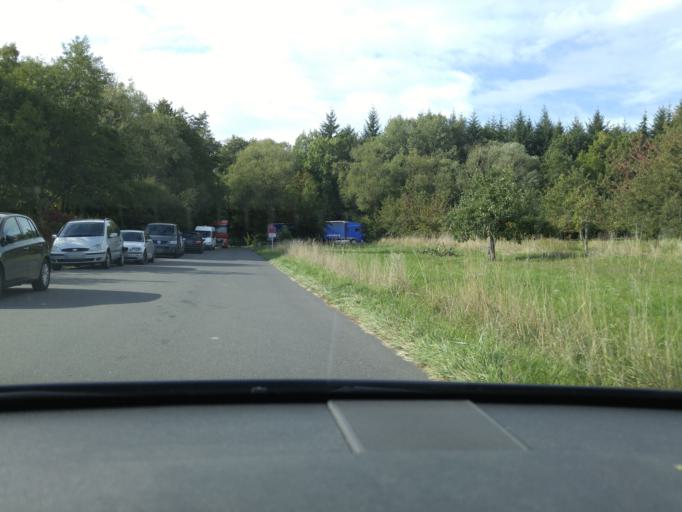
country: DE
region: Hesse
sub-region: Regierungsbezirk Darmstadt
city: Rosbach vor der Hohe
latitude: 50.3315
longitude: 8.7023
